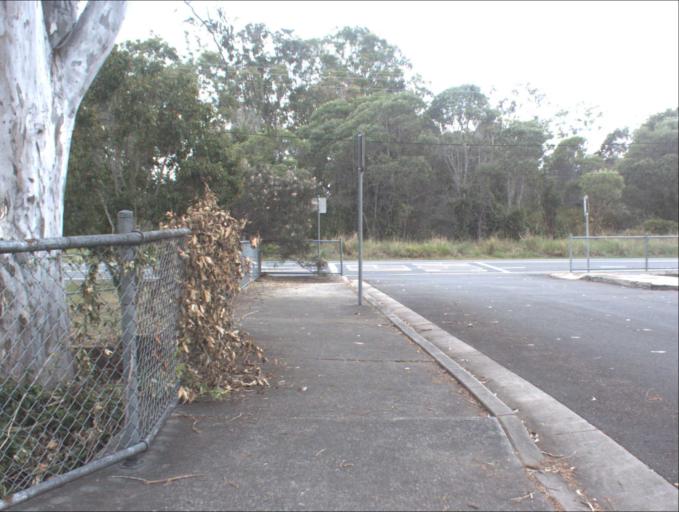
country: AU
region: Queensland
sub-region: Gold Coast
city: Yatala
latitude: -27.6778
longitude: 153.2354
